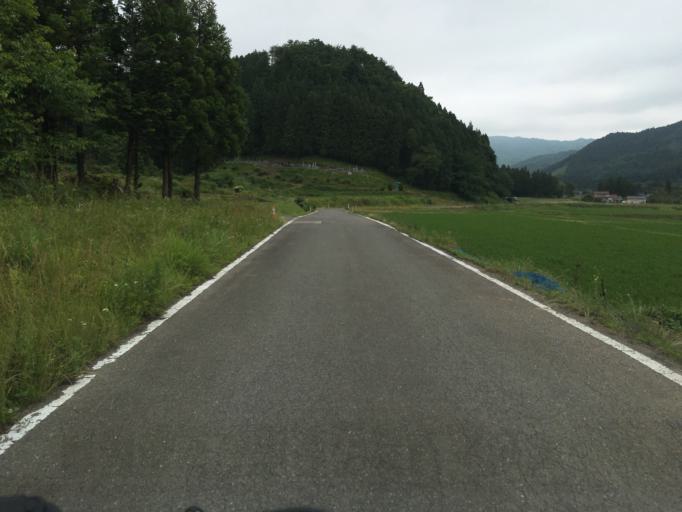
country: JP
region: Miyagi
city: Marumori
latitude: 37.7643
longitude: 140.8466
